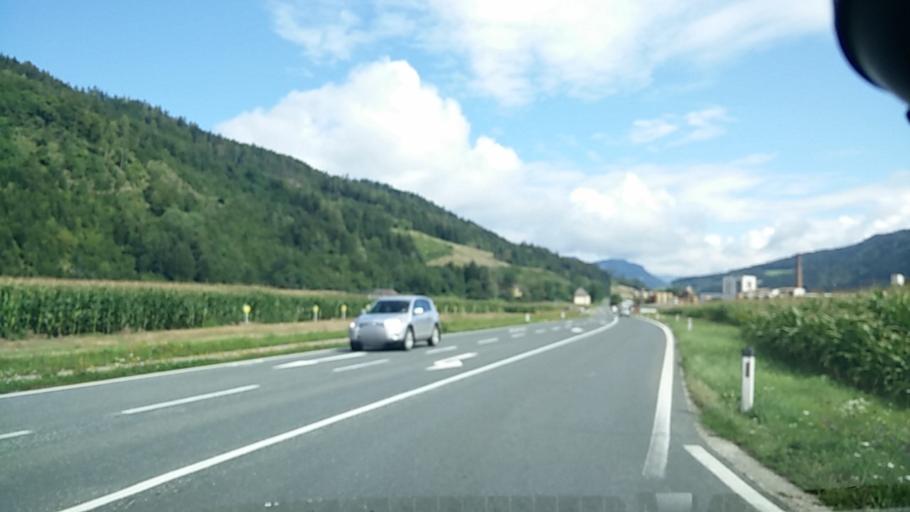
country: AT
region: Carinthia
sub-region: Politischer Bezirk Sankt Veit an der Glan
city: Bruckl
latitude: 46.7290
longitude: 14.5266
